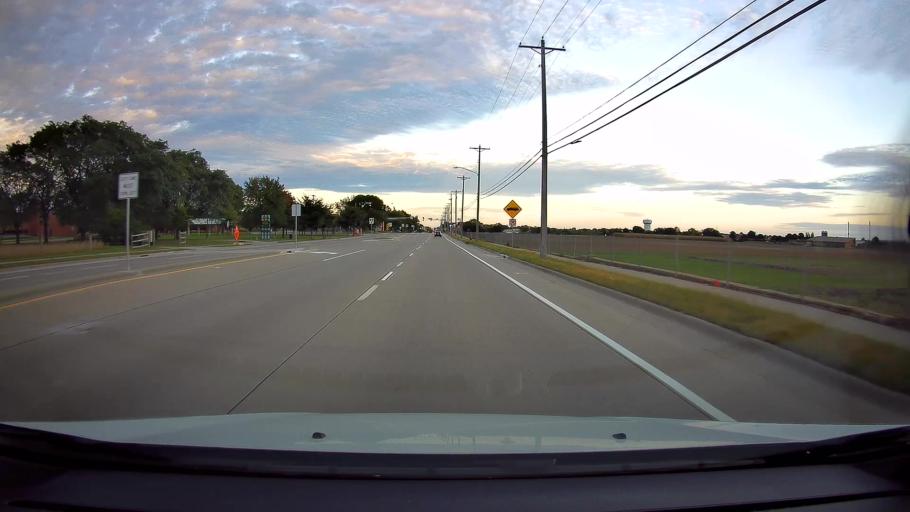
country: US
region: Minnesota
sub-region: Ramsey County
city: Falcon Heights
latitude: 44.9916
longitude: -93.1850
